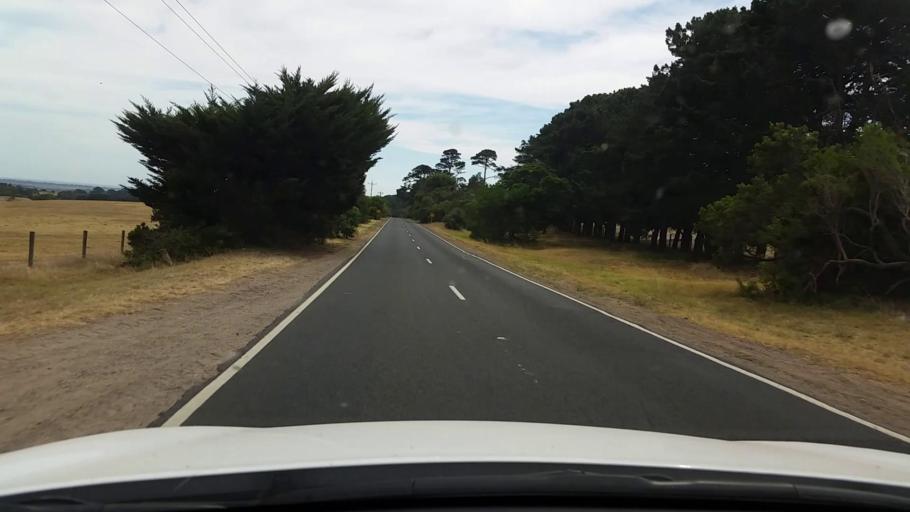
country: AU
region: Victoria
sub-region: Mornington Peninsula
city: Saint Andrews Beach
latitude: -38.4414
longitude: 144.8968
